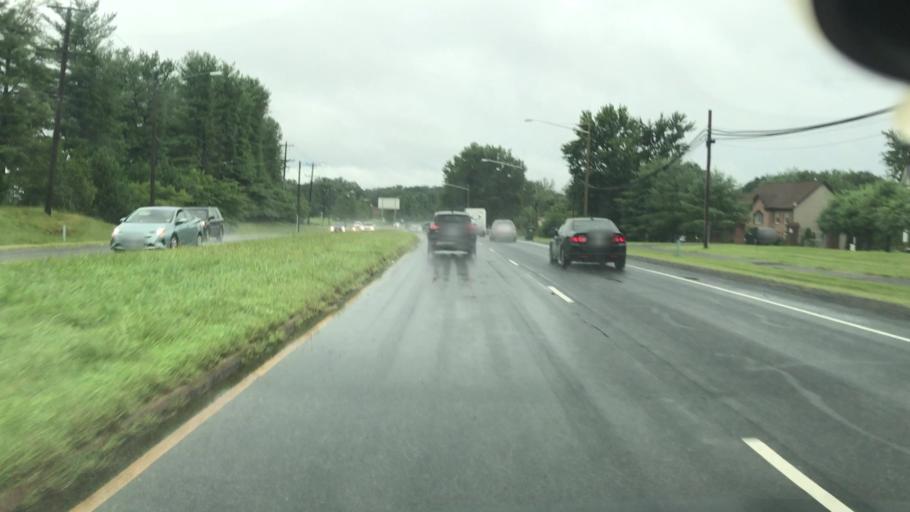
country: US
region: Virginia
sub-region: Fairfax County
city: Fairfax Station
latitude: 38.8169
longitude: -77.3208
